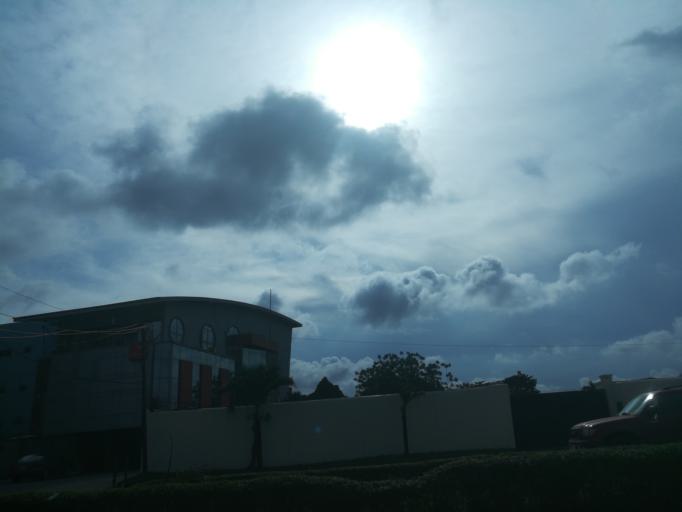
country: NG
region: Lagos
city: Ikeja
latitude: 6.6190
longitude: 3.3579
